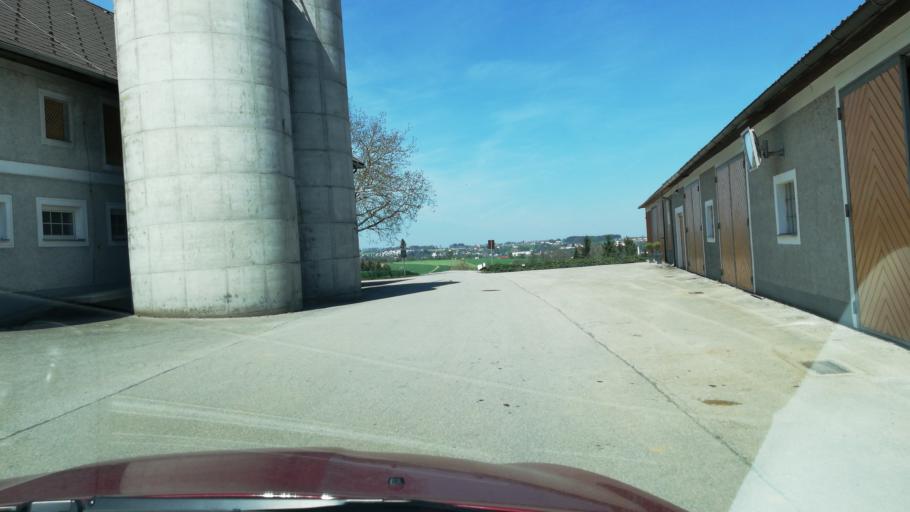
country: AT
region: Upper Austria
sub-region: Politischer Bezirk Steyr-Land
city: Pfarrkirchen bei Bad Hall
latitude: 48.0420
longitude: 14.1649
